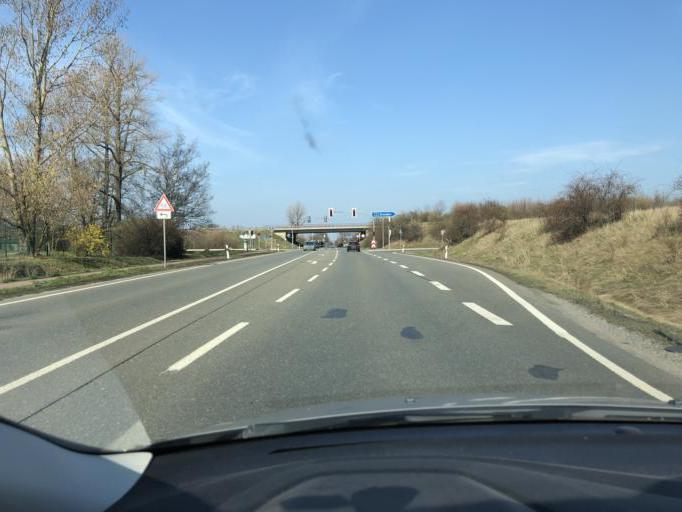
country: DE
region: Thuringia
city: Hetschburg
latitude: 50.9426
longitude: 11.2954
